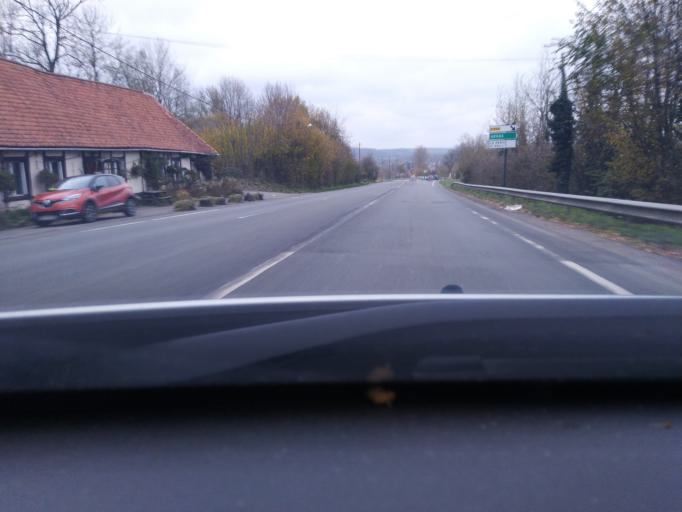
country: FR
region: Nord-Pas-de-Calais
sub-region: Departement du Pas-de-Calais
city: Hesdin
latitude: 50.3588
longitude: 2.0373
